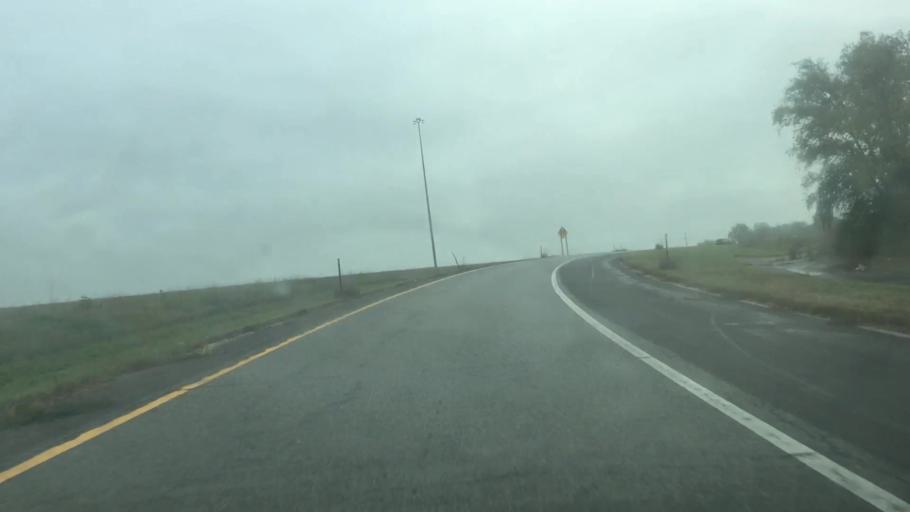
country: US
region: Kansas
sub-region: Wyandotte County
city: Edwardsville
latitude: 39.0078
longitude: -94.7834
